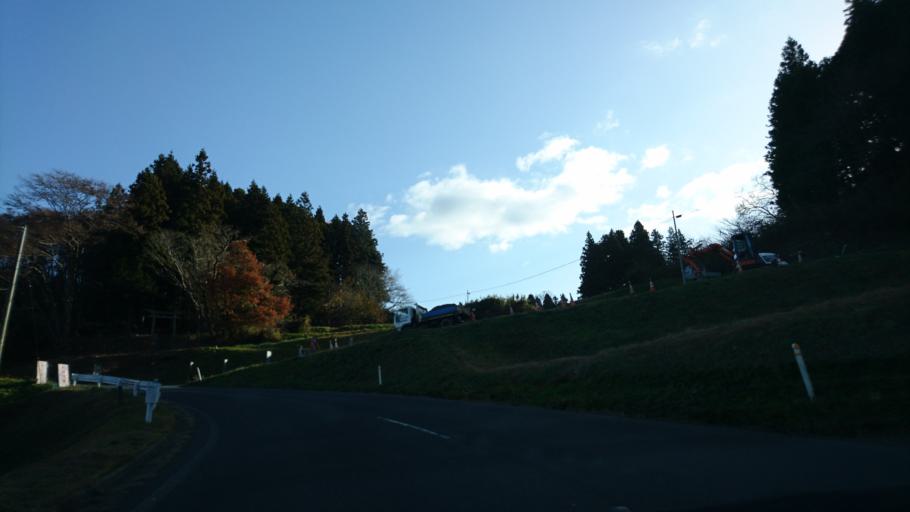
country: JP
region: Iwate
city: Ichinoseki
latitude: 38.8926
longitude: 141.2830
